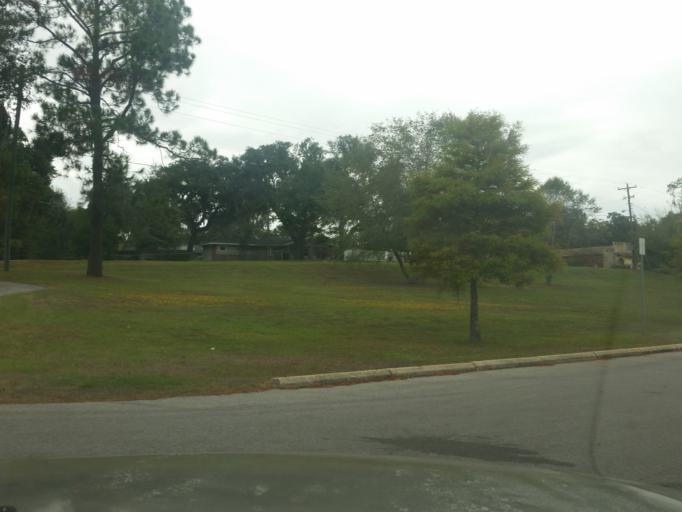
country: US
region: Florida
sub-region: Santa Rosa County
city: Milton
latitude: 30.6338
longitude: -87.0365
